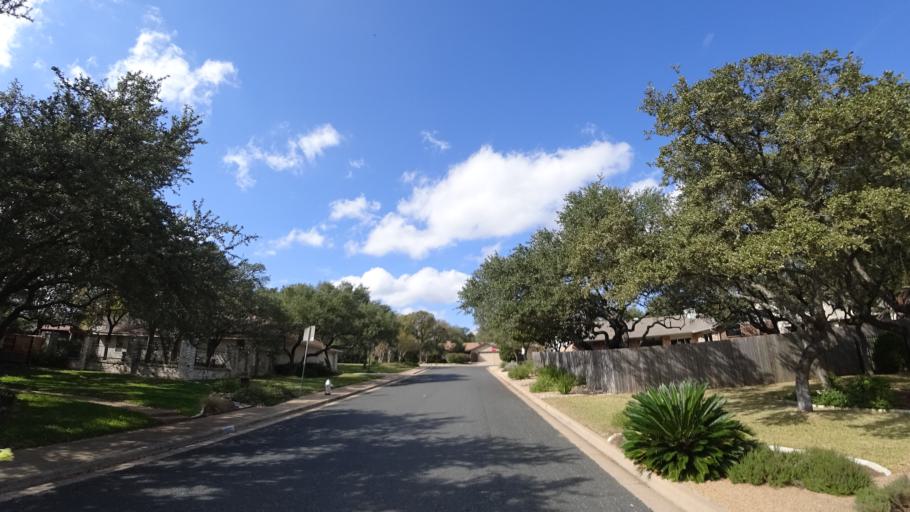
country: US
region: Texas
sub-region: Williamson County
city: Anderson Mill
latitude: 30.4245
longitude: -97.8041
